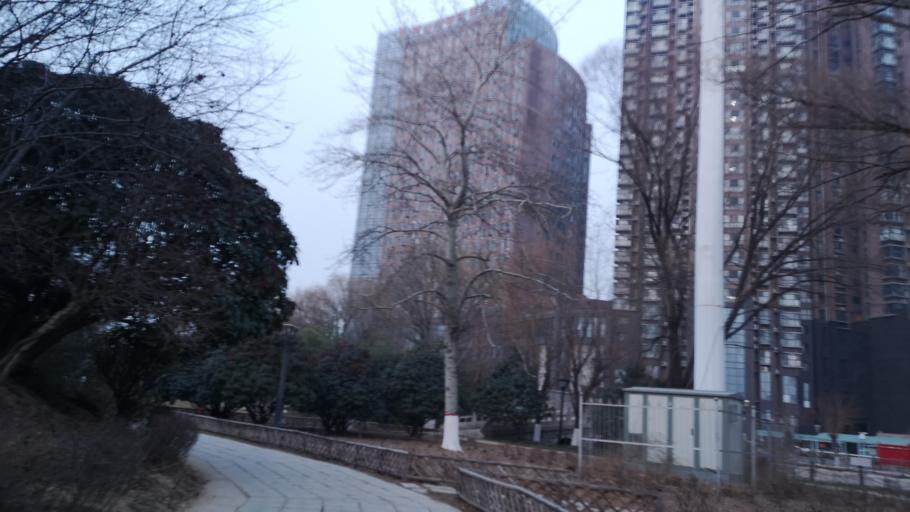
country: CN
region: Henan Sheng
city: Zhongyuanlu
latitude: 35.7733
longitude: 115.0789
